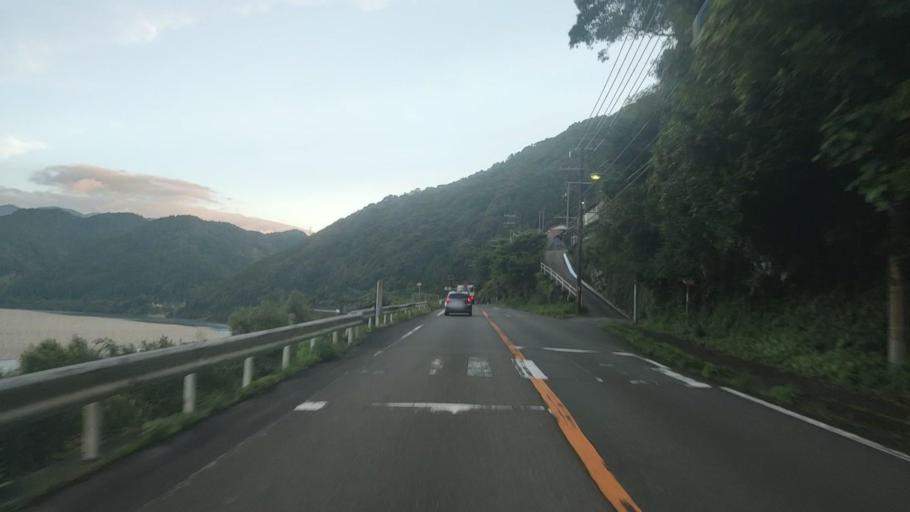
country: JP
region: Wakayama
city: Shingu
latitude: 33.8228
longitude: 135.8556
